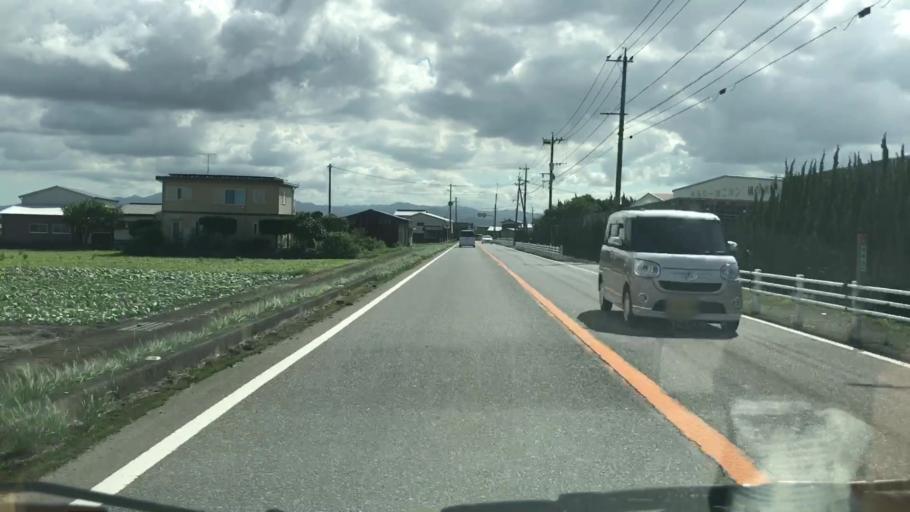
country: JP
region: Saga Prefecture
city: Kashima
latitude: 33.1754
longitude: 130.1832
